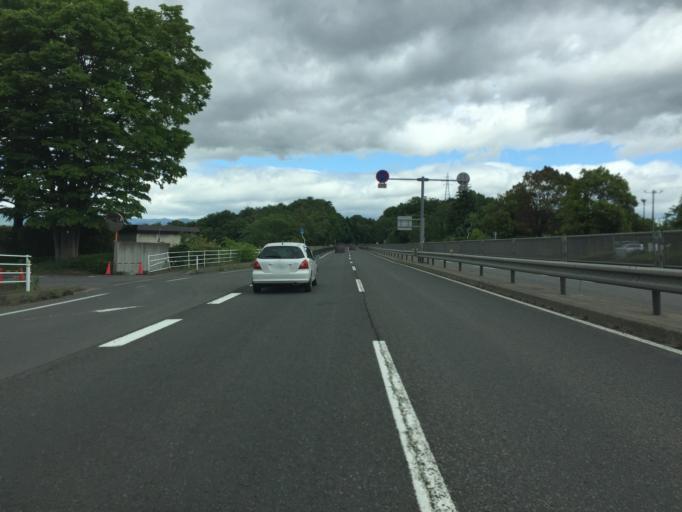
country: JP
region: Fukushima
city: Fukushima-shi
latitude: 37.6956
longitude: 140.4606
